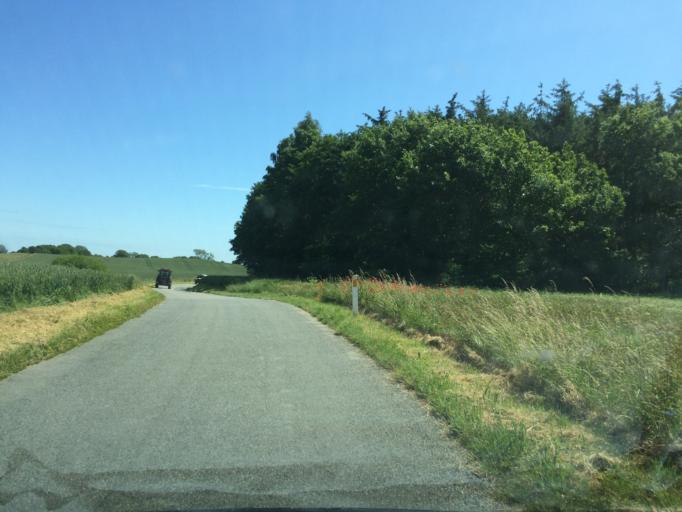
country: DK
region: Central Jutland
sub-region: Samso Kommune
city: Tranebjerg
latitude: 55.8299
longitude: 10.5518
